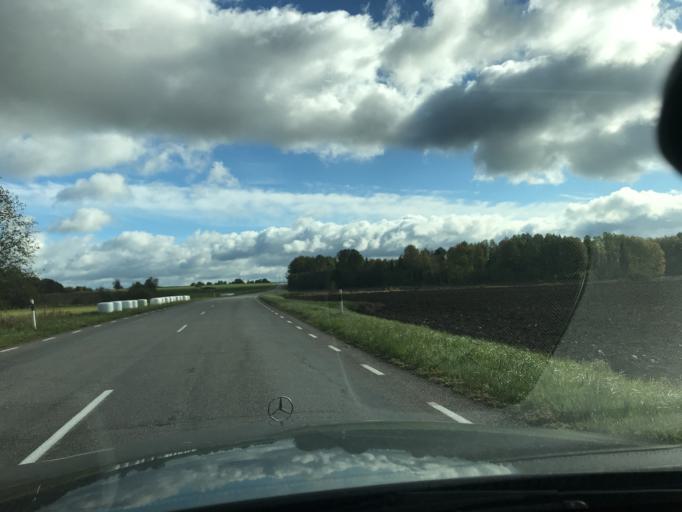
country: EE
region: Vorumaa
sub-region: Antsla vald
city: Vana-Antsla
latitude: 57.9044
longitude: 26.4571
